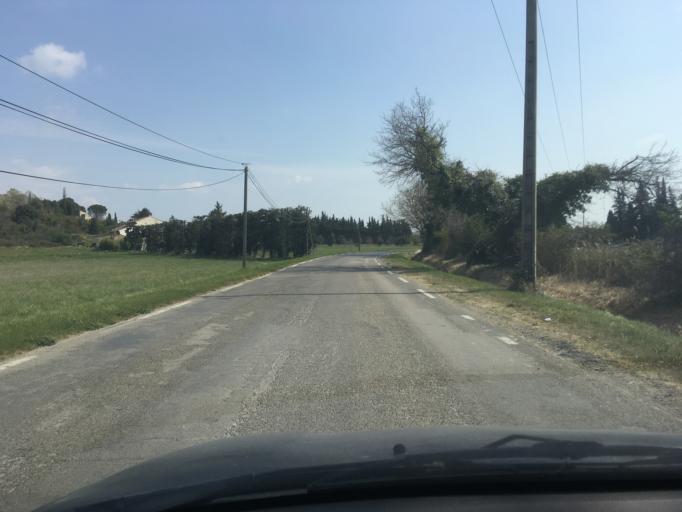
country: FR
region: Provence-Alpes-Cote d'Azur
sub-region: Departement du Vaucluse
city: Aubignan
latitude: 44.1001
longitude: 5.0131
